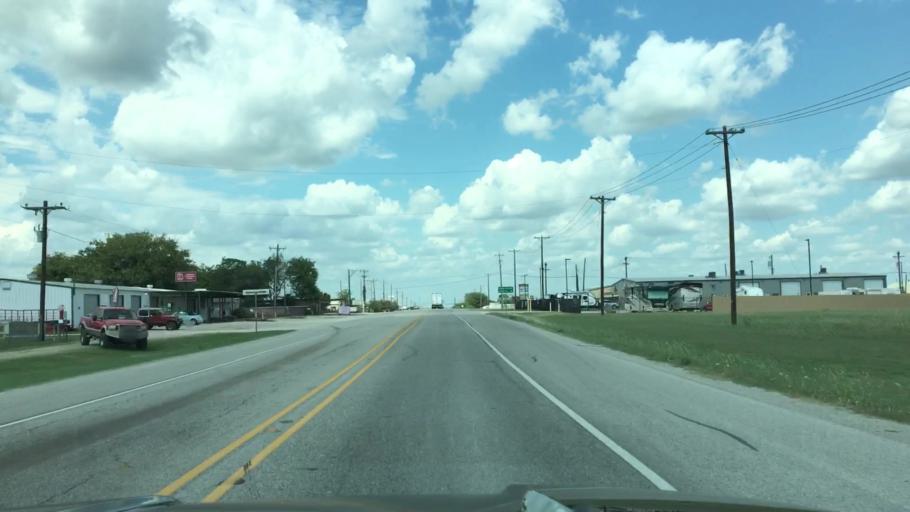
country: US
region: Texas
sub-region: Tarrant County
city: Pecan Acres
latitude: 32.9483
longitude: -97.4208
